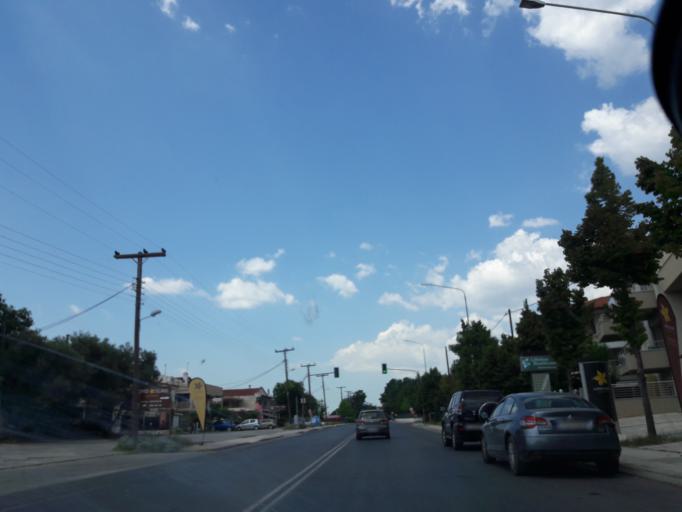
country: GR
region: Central Macedonia
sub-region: Nomos Thessalonikis
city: Agia Paraskevi
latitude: 40.5224
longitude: 23.0544
